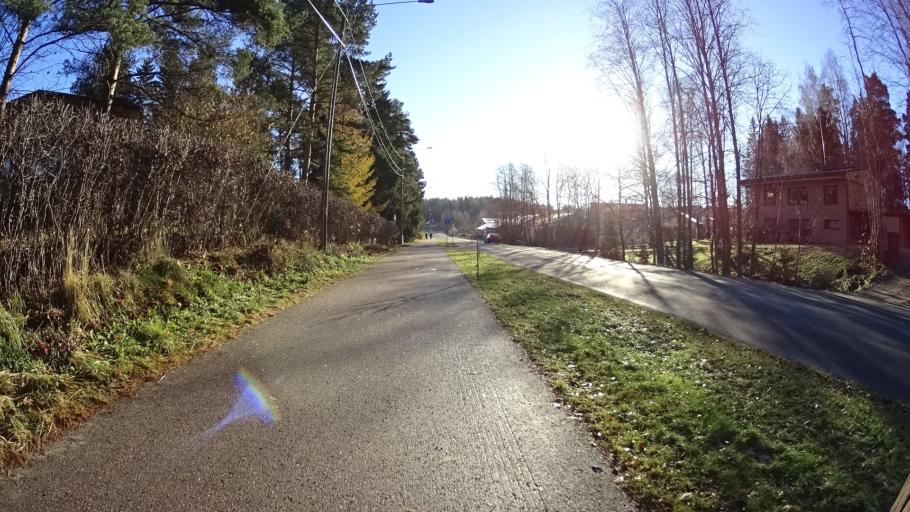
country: FI
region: Uusimaa
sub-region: Helsinki
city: Kilo
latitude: 60.2395
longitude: 24.7676
